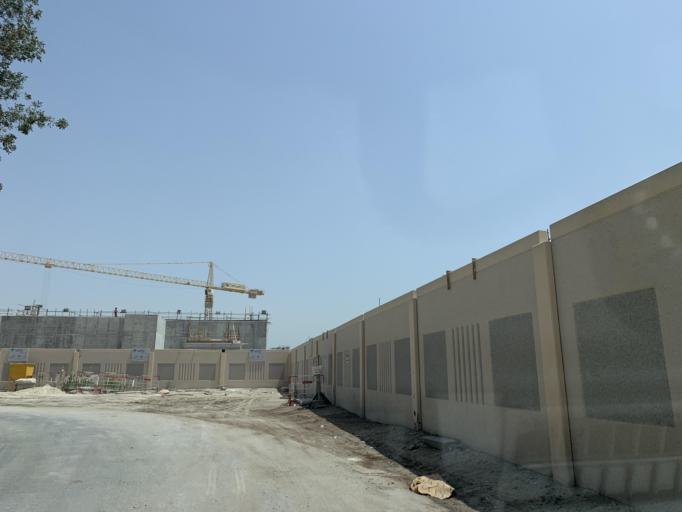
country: BH
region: Northern
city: Madinat `Isa
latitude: 26.1955
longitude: 50.5499
